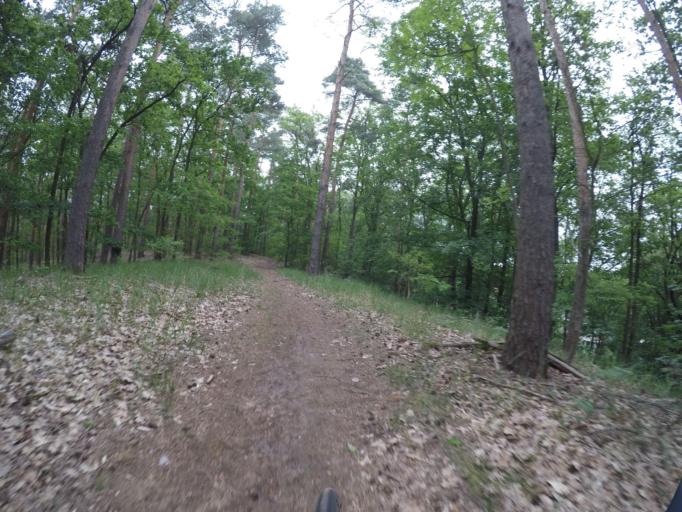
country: DE
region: Berlin
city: Tegel
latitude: 52.6030
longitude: 13.2880
